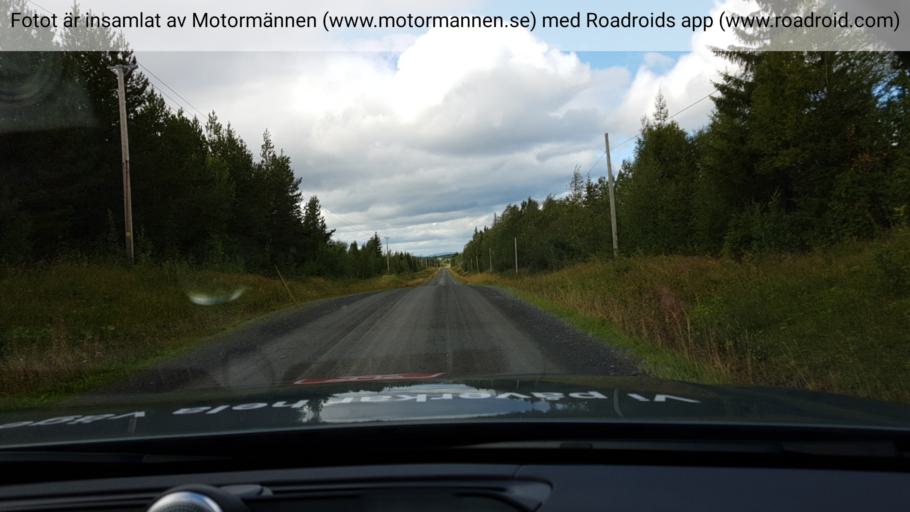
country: SE
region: Jaemtland
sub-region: OEstersunds Kommun
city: Lit
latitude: 63.6247
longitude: 14.9758
